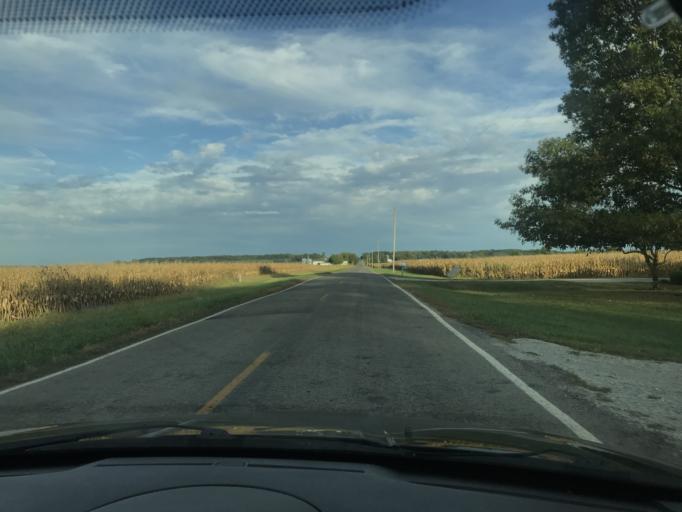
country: US
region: Ohio
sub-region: Logan County
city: West Liberty
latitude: 40.1946
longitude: -83.7961
